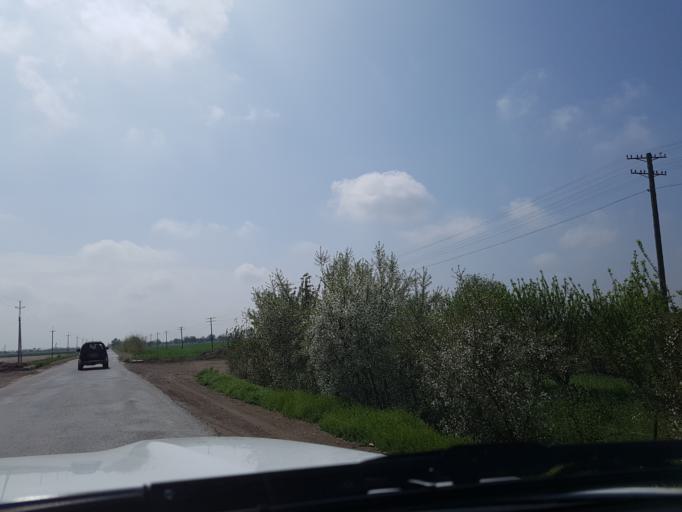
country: TM
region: Lebap
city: Turkmenabat
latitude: 38.9616
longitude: 63.6780
